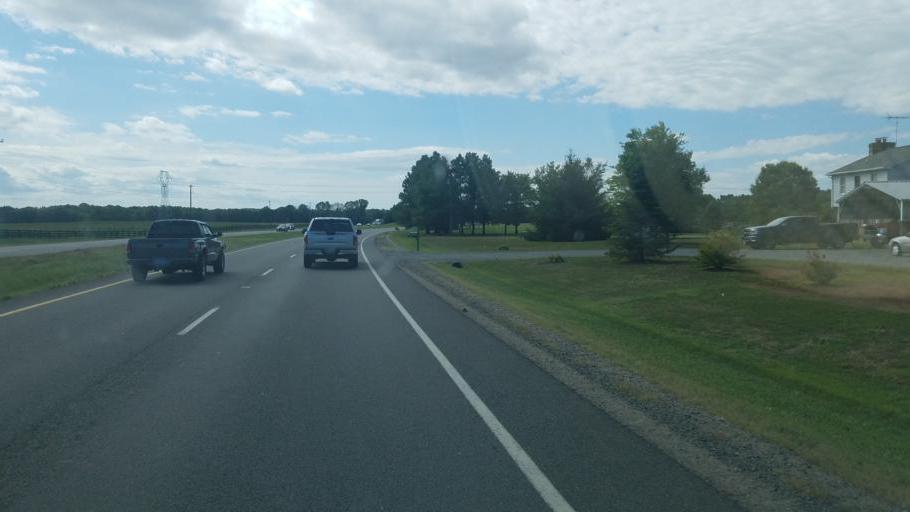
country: US
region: Virginia
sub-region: Fauquier County
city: Bealeton
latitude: 38.5561
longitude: -77.7350
